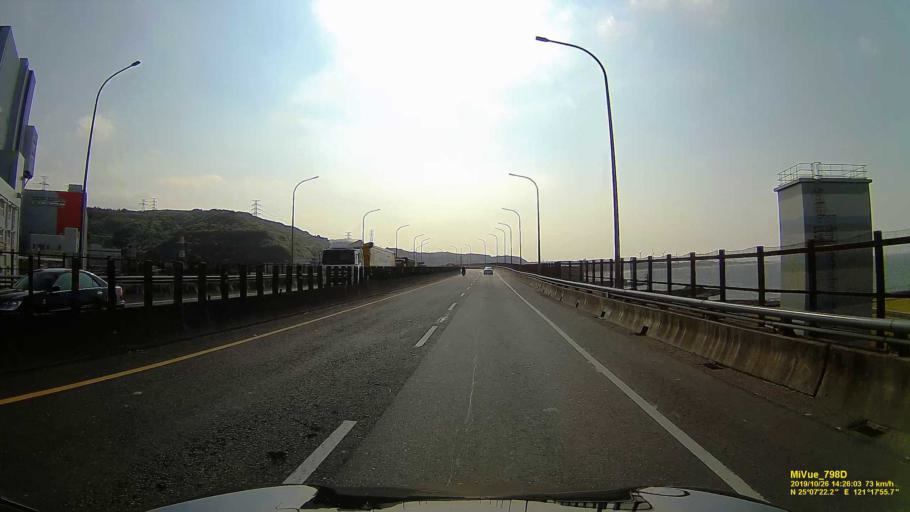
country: TW
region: Taiwan
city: Taoyuan City
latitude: 25.1227
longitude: 121.2986
